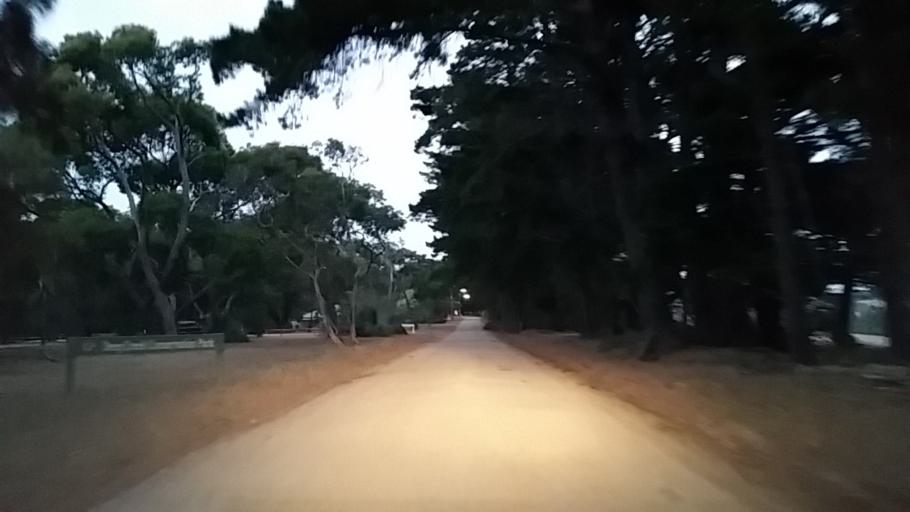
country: AU
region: South Australia
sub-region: Yankalilla
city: Normanville
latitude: -35.6299
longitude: 138.1958
